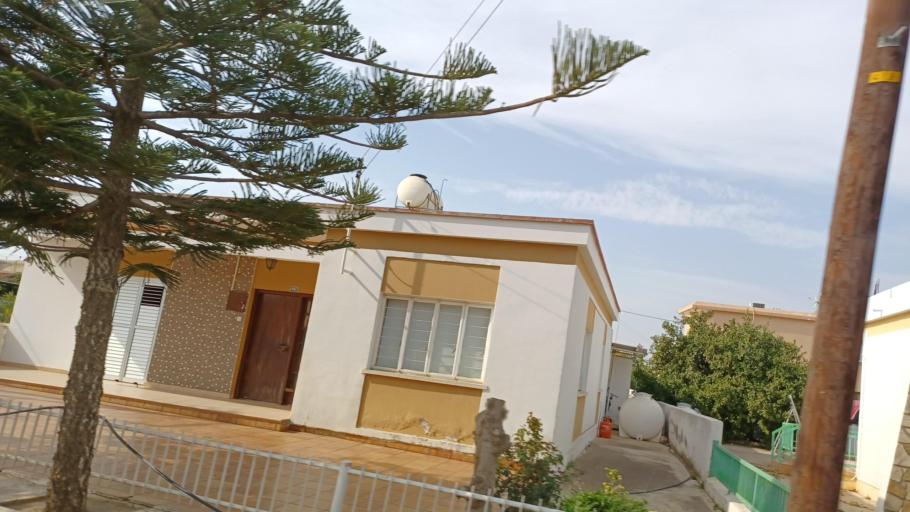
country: CY
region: Ammochostos
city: Frenaros
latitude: 35.0389
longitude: 33.9194
